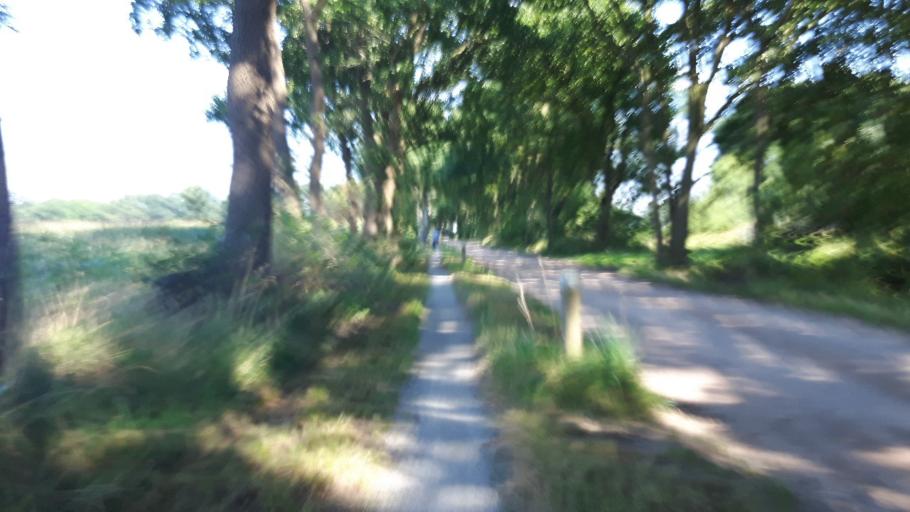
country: NL
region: Drenthe
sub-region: Gemeente Tynaarlo
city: Tynaarlo
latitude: 53.1206
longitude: 6.5971
